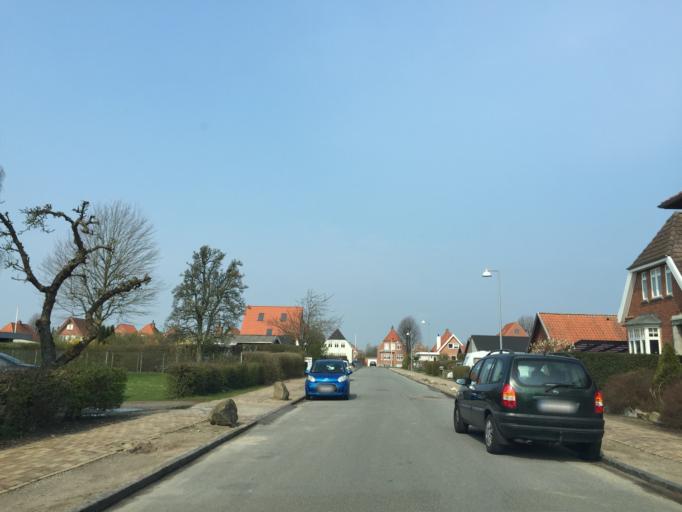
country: DK
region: South Denmark
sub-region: Odense Kommune
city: Odense
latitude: 55.4171
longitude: 10.3995
